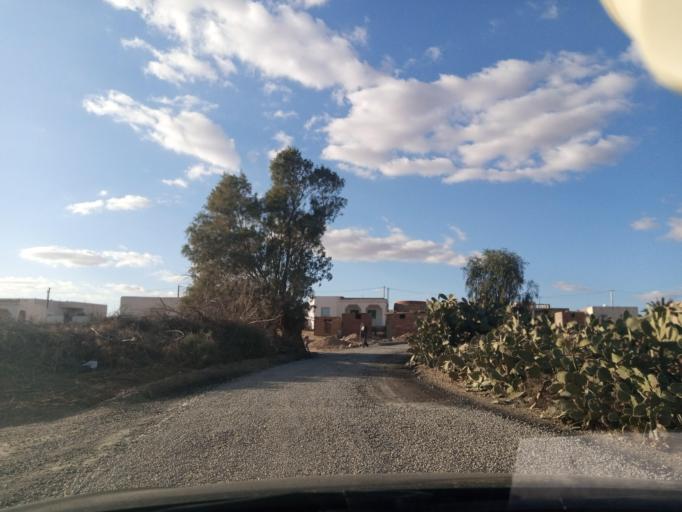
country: TN
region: Safaqis
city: Bi'r `Ali Bin Khalifah
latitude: 34.7110
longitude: 10.4230
